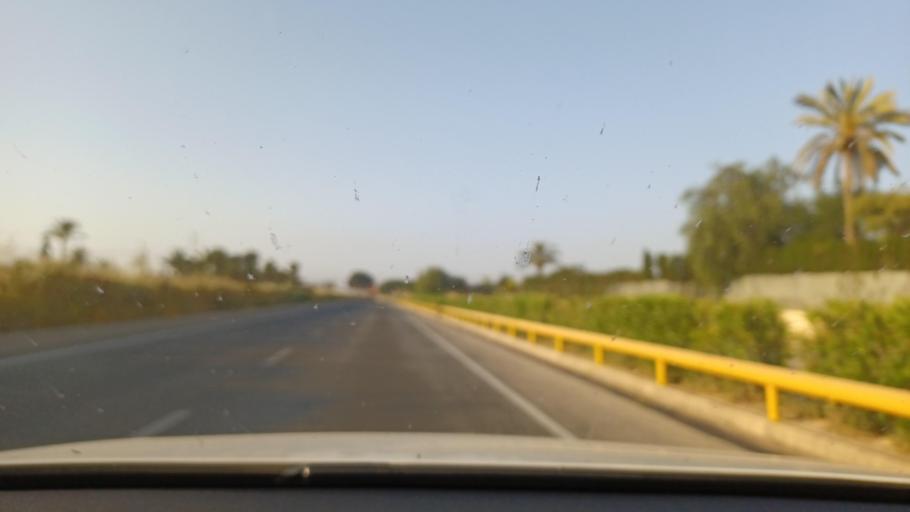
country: ES
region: Valencia
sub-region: Provincia de Alicante
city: Elche
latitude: 38.2188
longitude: -0.6972
